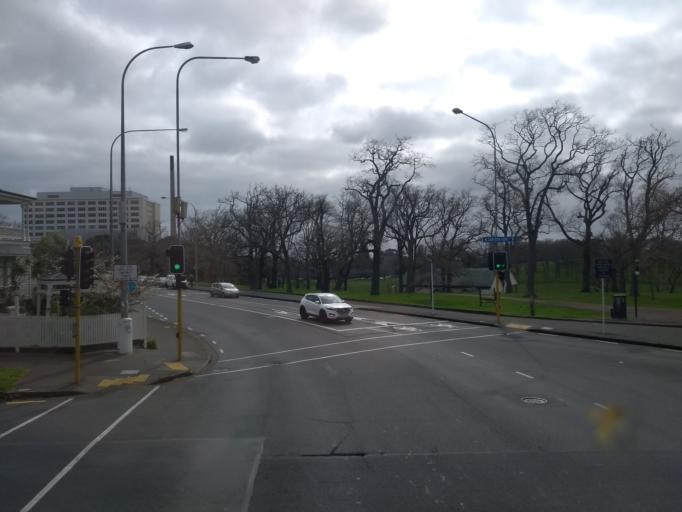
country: NZ
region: Auckland
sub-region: Auckland
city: Auckland
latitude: -36.8642
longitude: 174.7710
